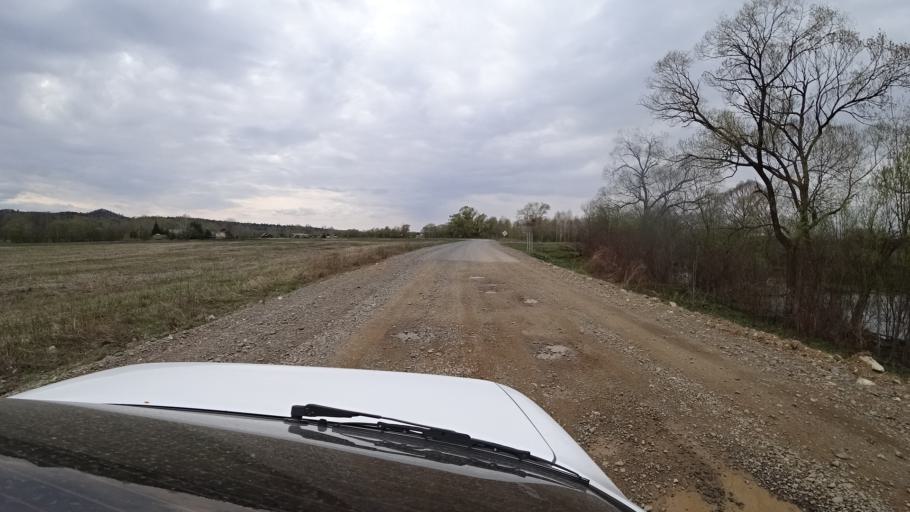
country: RU
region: Primorskiy
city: Novopokrovka
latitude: 45.4914
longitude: 134.4548
